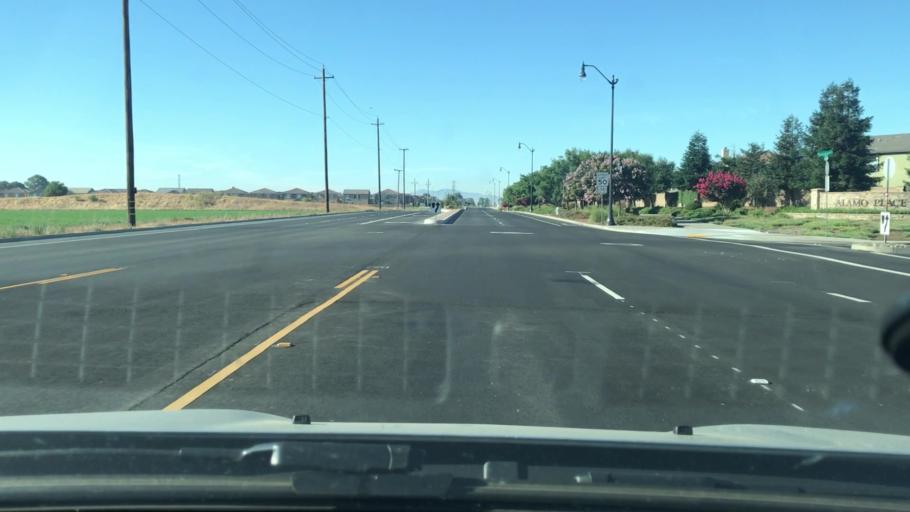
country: US
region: California
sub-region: Solano County
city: Vacaville
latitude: 38.3330
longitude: -121.9340
